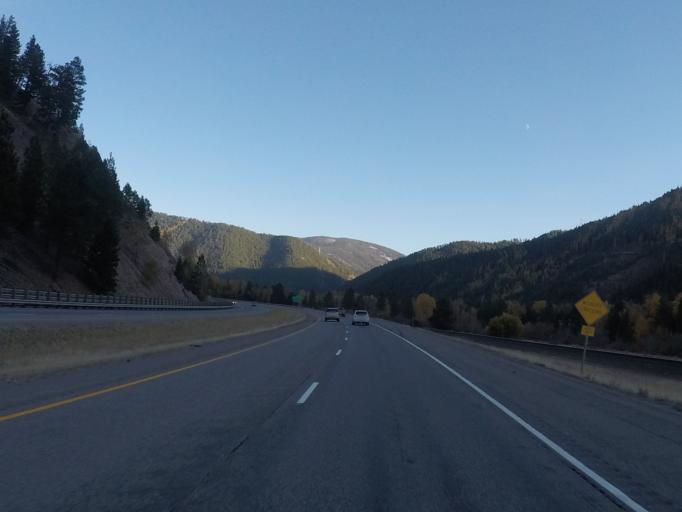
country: US
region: Montana
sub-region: Missoula County
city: Clinton
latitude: 46.7298
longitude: -113.6957
